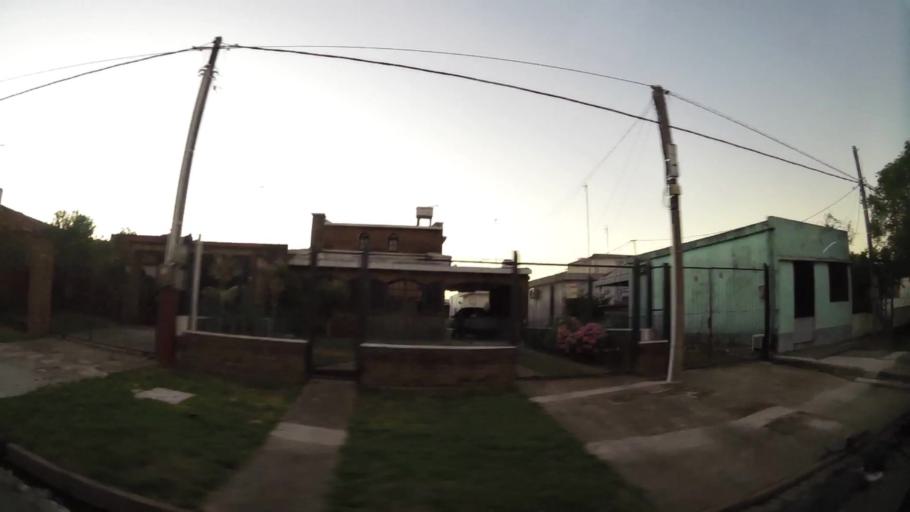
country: UY
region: Canelones
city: Toledo
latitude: -34.8160
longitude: -56.1404
